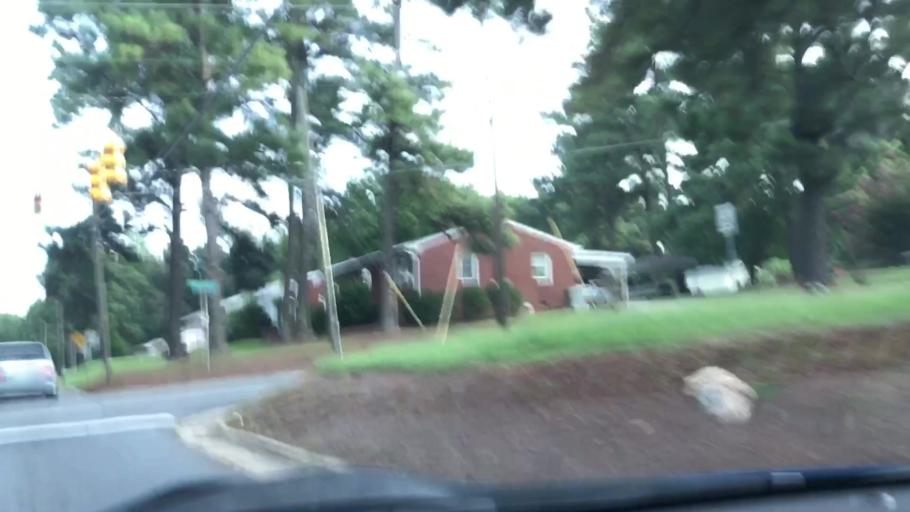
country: US
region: North Carolina
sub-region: Randolph County
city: Asheboro
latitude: 35.7157
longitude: -79.8064
